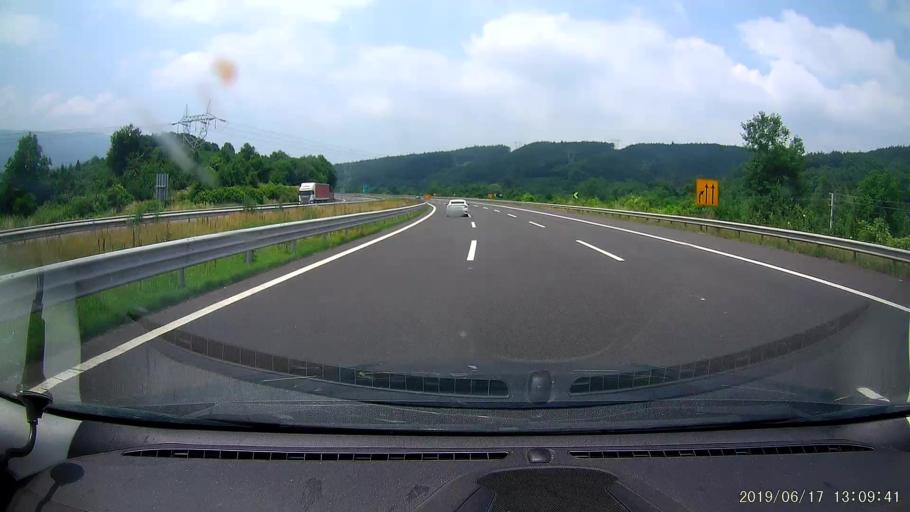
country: TR
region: Duzce
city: Kaynasli
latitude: 40.7917
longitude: 31.2882
